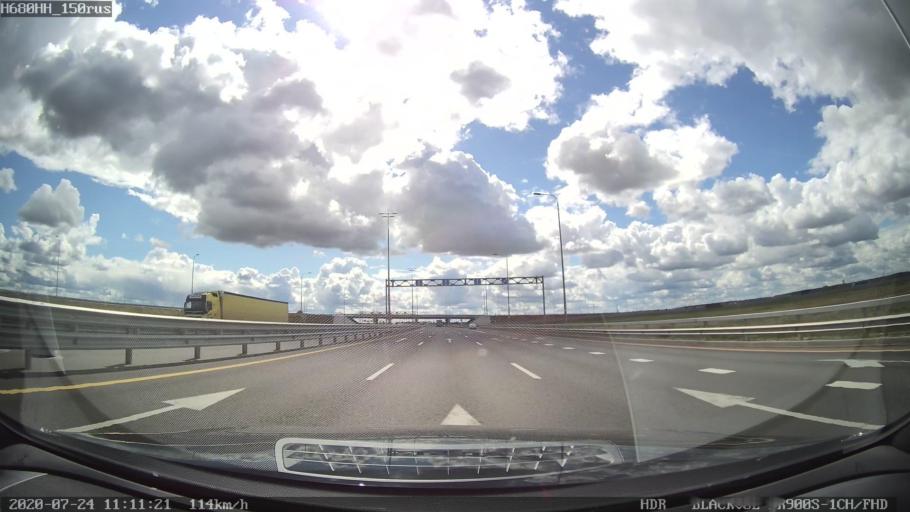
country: RU
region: St.-Petersburg
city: Tyarlevo
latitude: 59.7240
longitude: 30.5141
